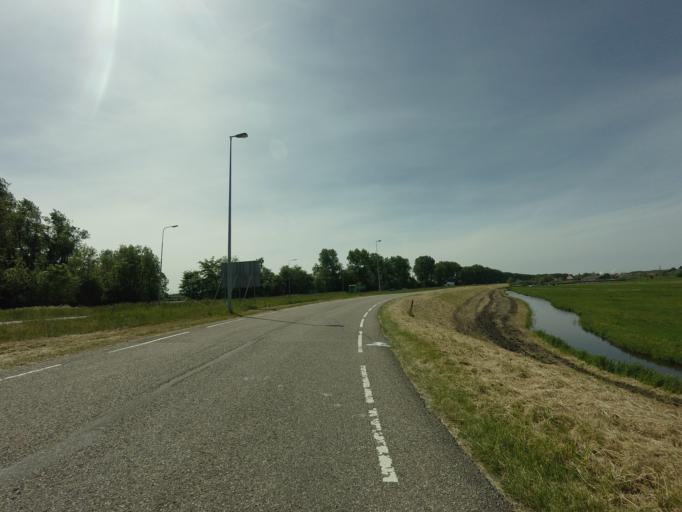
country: NL
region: North Holland
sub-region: Gemeente Velsen
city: Velsen-Zuid
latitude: 52.4362
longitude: 4.7247
